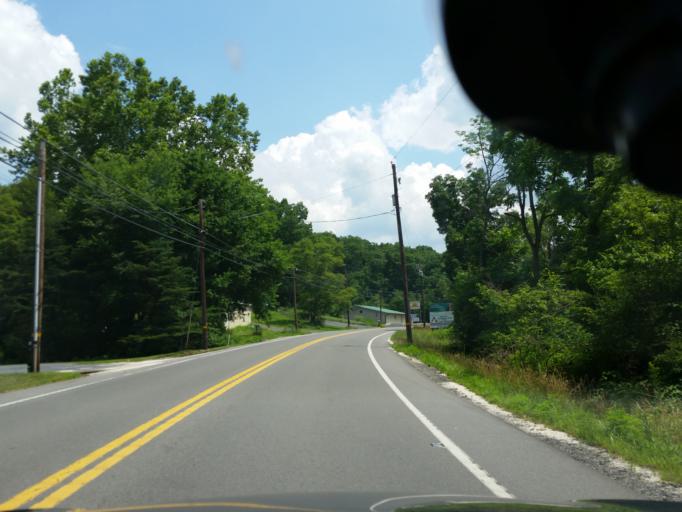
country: US
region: Pennsylvania
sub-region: Cumberland County
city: Schlusser
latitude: 40.3170
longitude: -77.1582
